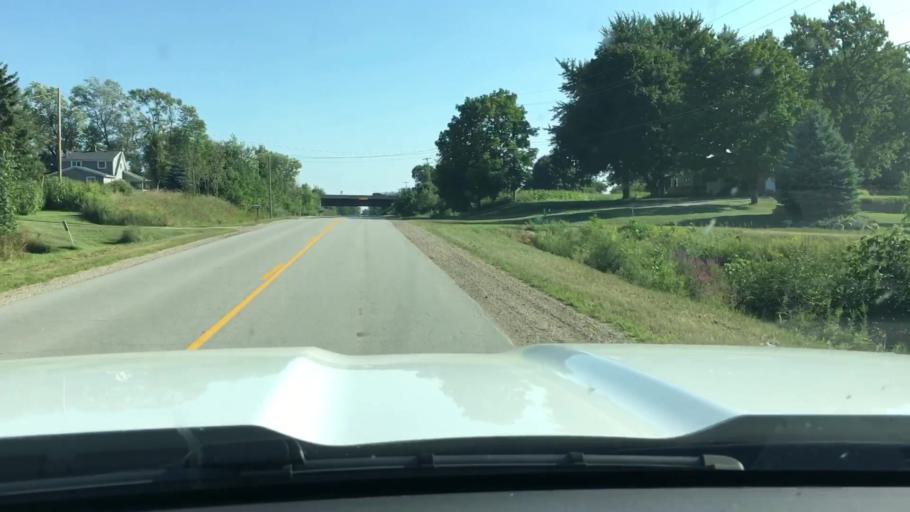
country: US
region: Michigan
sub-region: Ottawa County
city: Zeeland
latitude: 42.8237
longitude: -85.9401
